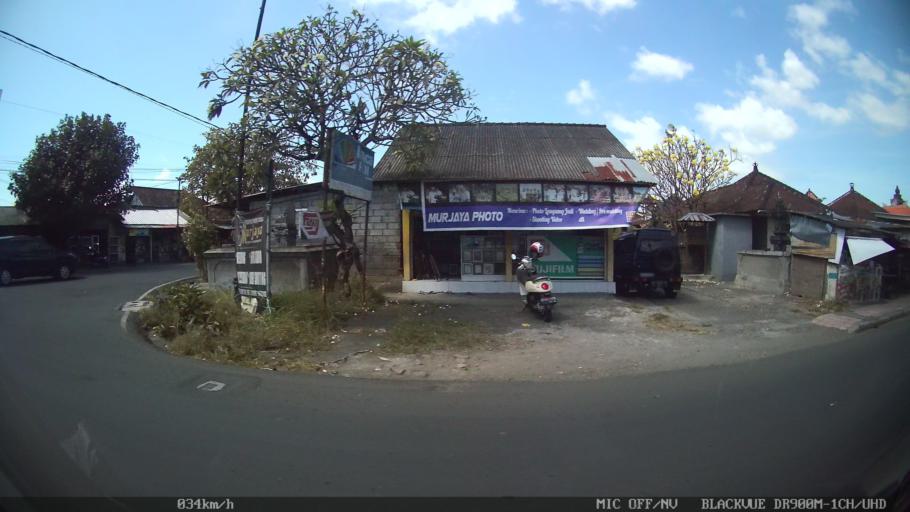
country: ID
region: Bali
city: Banjar Kertasari
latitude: -8.6317
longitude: 115.1833
